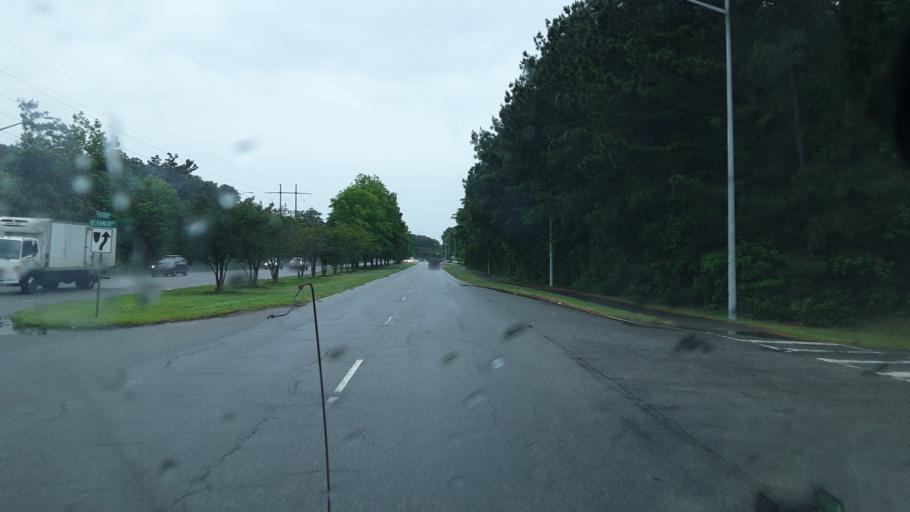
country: US
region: Virginia
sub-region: City of Virginia Beach
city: Virginia Beach
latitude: 36.7977
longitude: -75.9943
